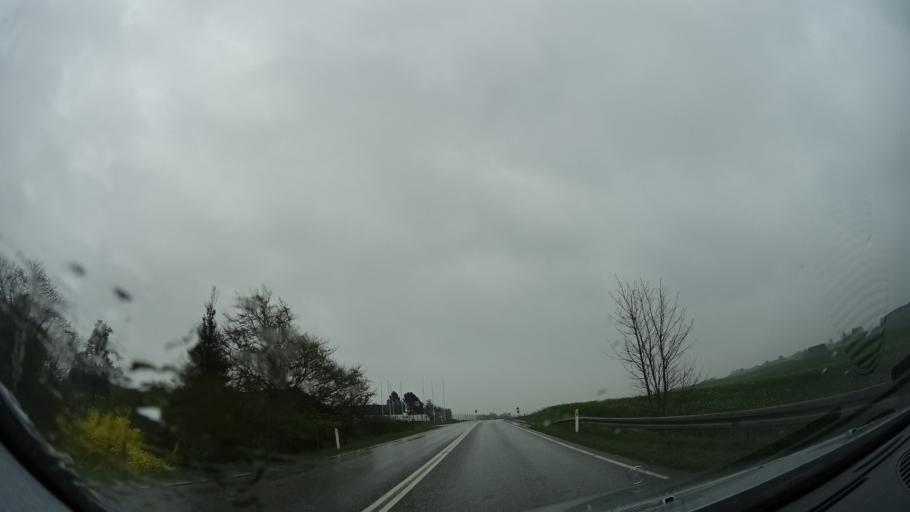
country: DK
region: Zealand
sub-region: Odsherred Kommune
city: Asnaes
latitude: 55.8035
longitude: 11.5984
